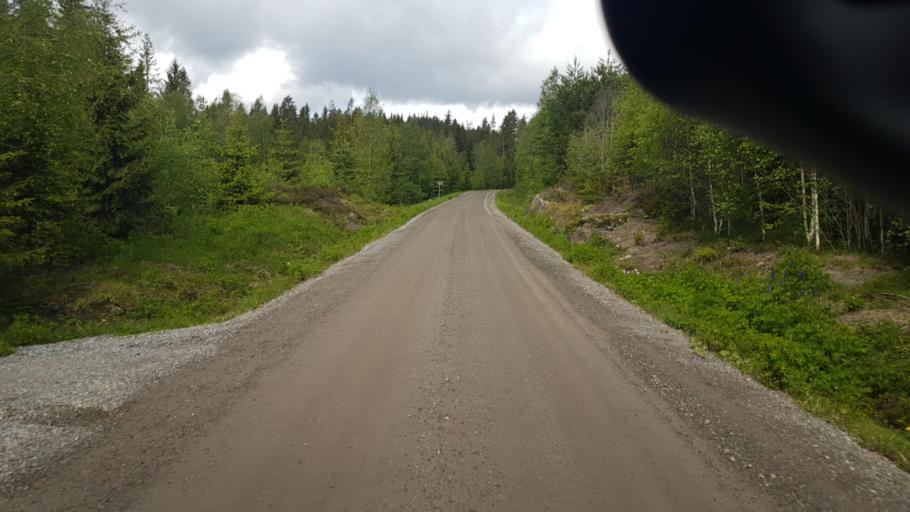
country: NO
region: Ostfold
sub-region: Romskog
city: Romskog
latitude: 59.7051
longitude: 12.0505
